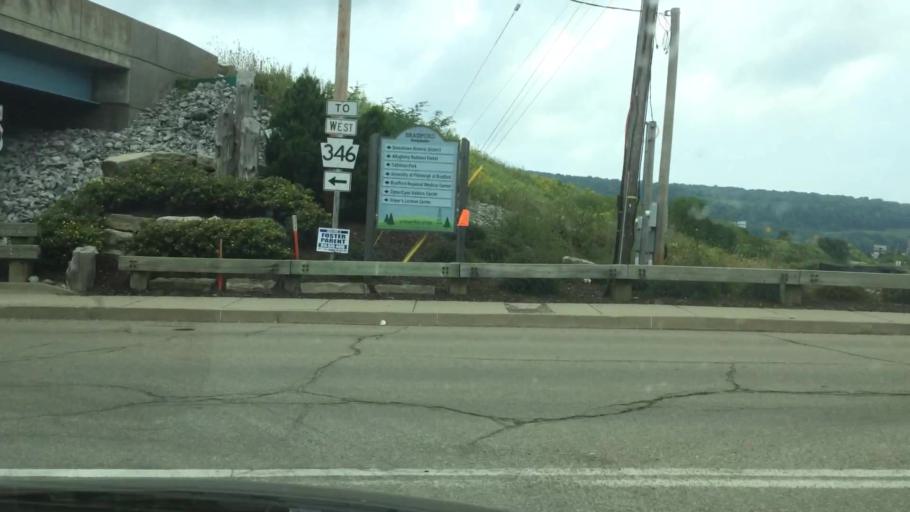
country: US
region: Pennsylvania
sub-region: McKean County
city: Bradford
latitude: 41.9526
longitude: -78.6457
